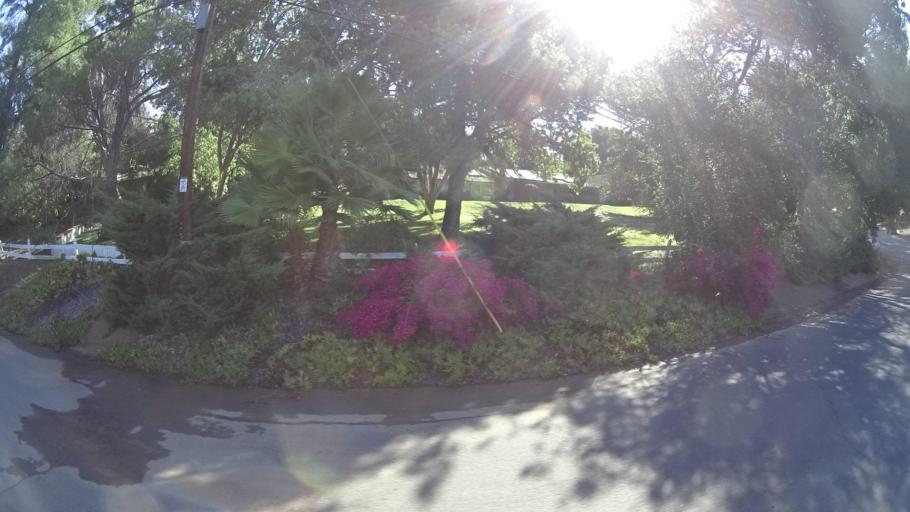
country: US
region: California
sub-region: San Diego County
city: Escondido
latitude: 33.0735
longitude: -117.0834
